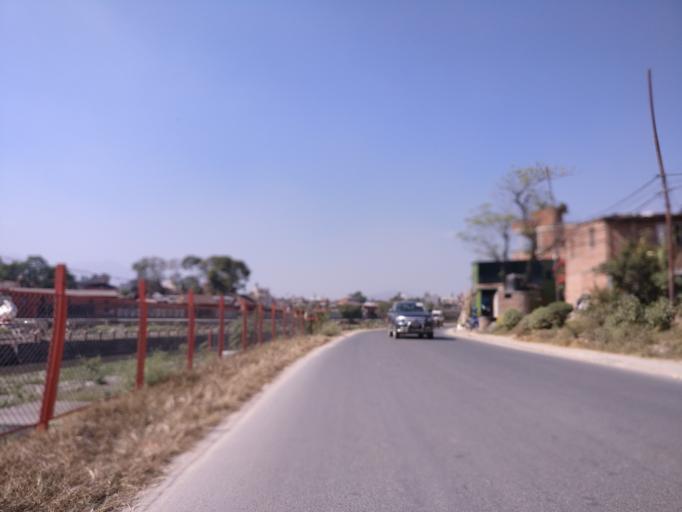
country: NP
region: Central Region
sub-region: Bagmati Zone
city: Patan
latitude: 27.6800
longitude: 85.3324
